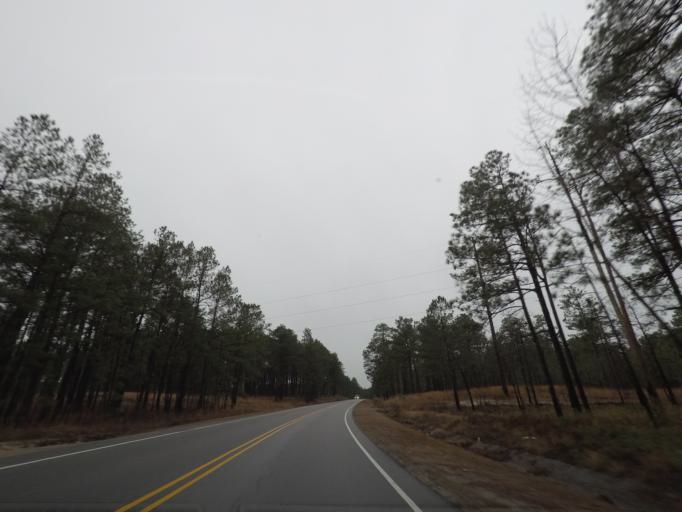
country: US
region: North Carolina
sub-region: Cumberland County
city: Spring Lake
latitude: 35.2369
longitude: -79.0103
